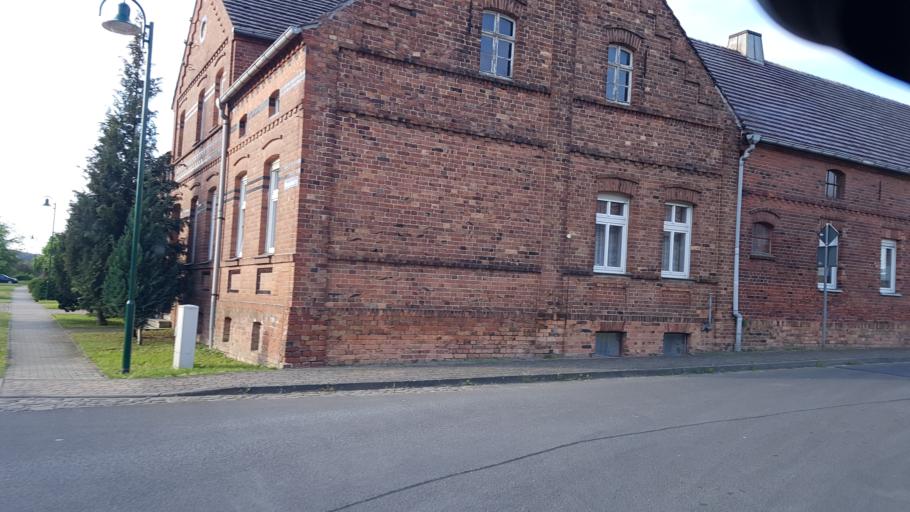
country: DE
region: Brandenburg
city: Dahme
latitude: 51.8630
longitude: 13.4618
